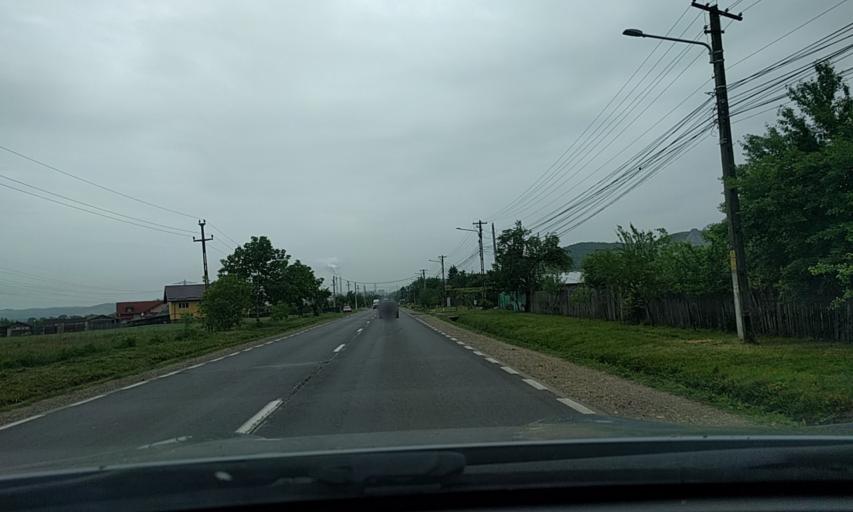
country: RO
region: Dambovita
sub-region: Comuna Aninoasa
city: Aninoasa
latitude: 44.9707
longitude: 25.4320
